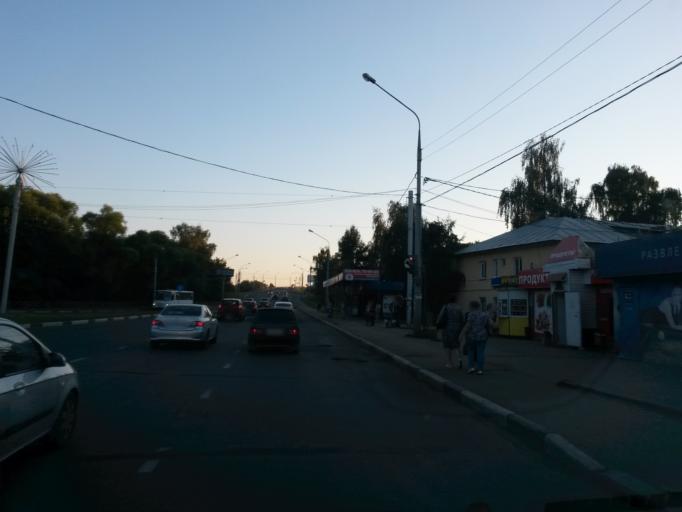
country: RU
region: Jaroslavl
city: Yaroslavl
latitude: 57.6451
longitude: 39.9067
